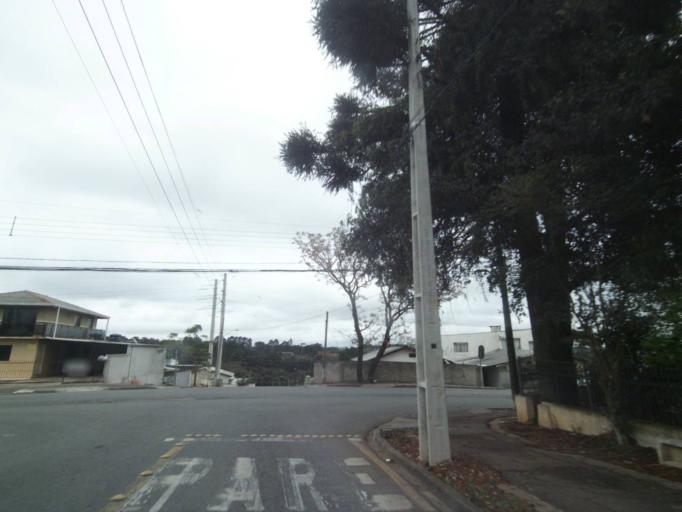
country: BR
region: Parana
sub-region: Sao Jose Dos Pinhais
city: Sao Jose dos Pinhais
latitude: -25.5203
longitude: -49.3051
